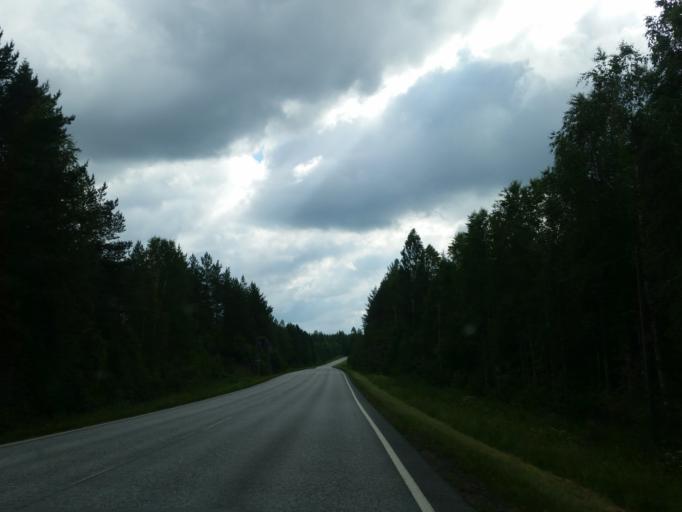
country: FI
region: Northern Savo
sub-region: Kuopio
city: Karttula
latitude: 62.8577
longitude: 27.2236
